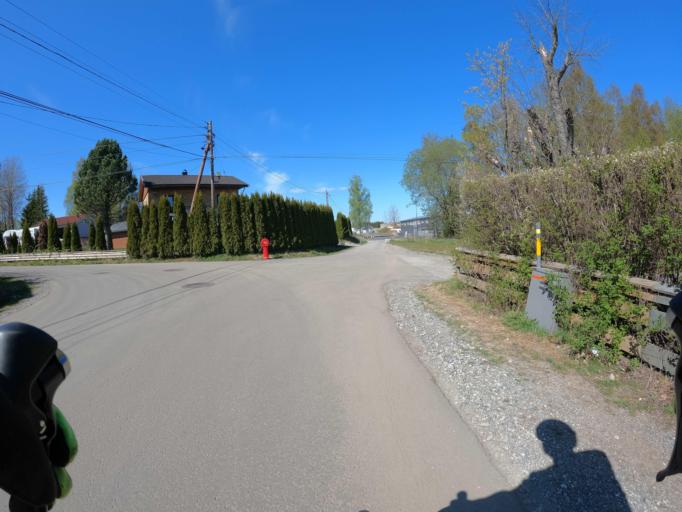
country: NO
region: Akershus
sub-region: Skedsmo
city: Leirsund
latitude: 60.0058
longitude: 11.0427
